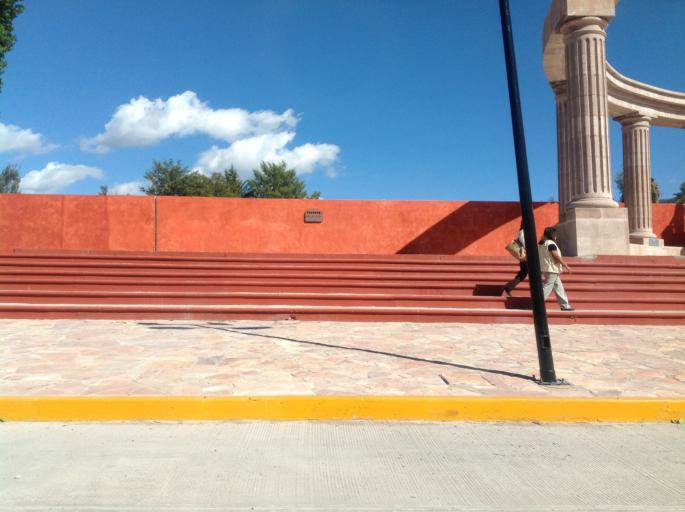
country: MX
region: Oaxaca
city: Ciudad de Huajuapam de Leon
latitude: 17.8129
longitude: -97.7670
